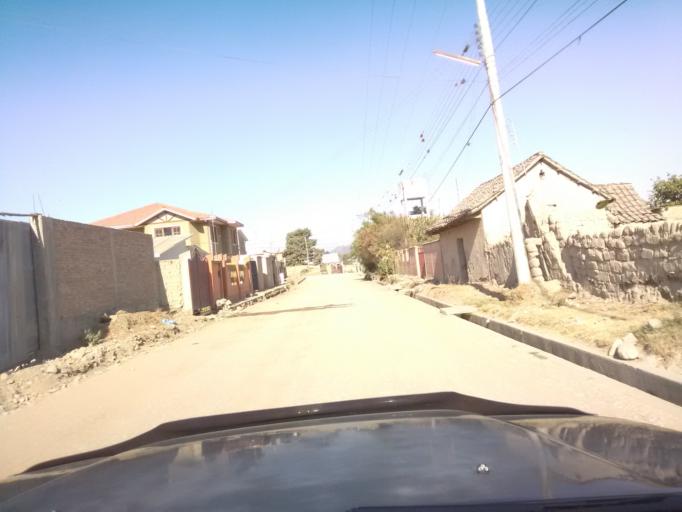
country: BO
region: Cochabamba
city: Cochabamba
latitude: -17.3600
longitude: -66.2001
